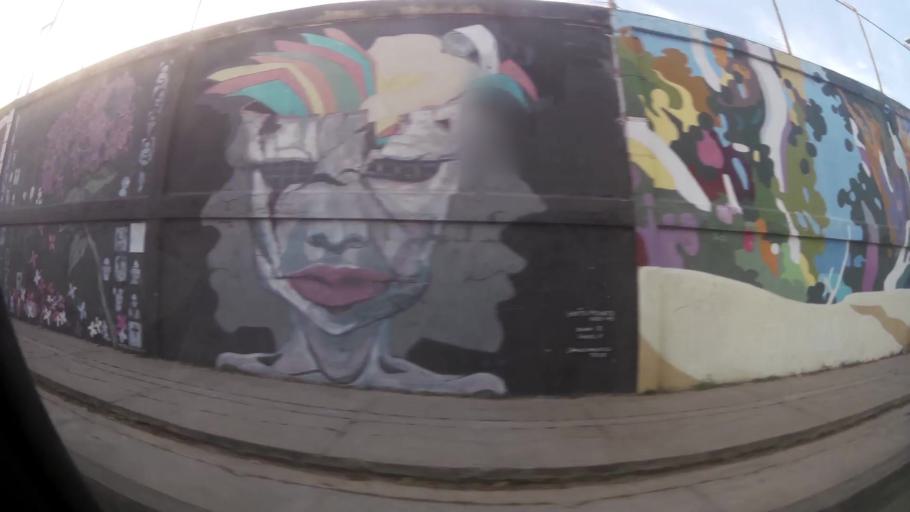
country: CO
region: Atlantico
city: Barranquilla
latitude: 10.9533
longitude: -74.8215
